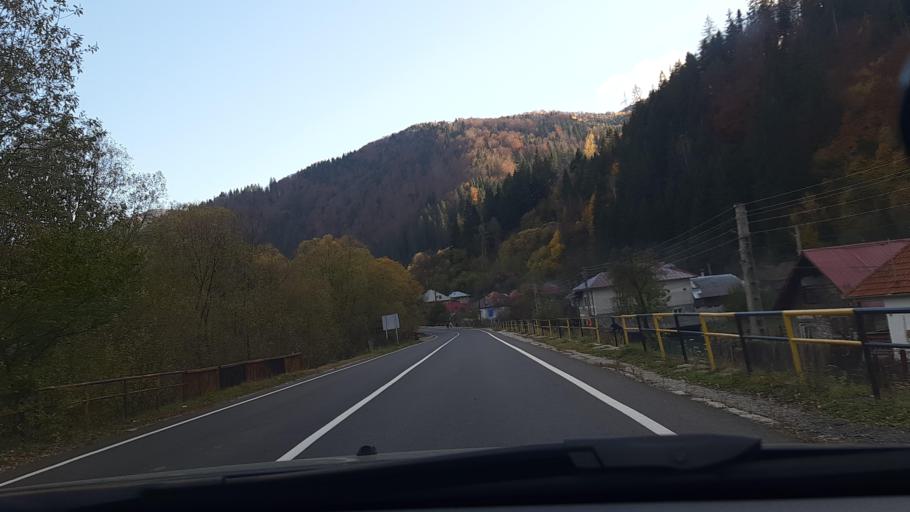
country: RO
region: Valcea
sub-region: Comuna Voineasa
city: Voineasa
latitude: 45.4169
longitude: 23.9598
